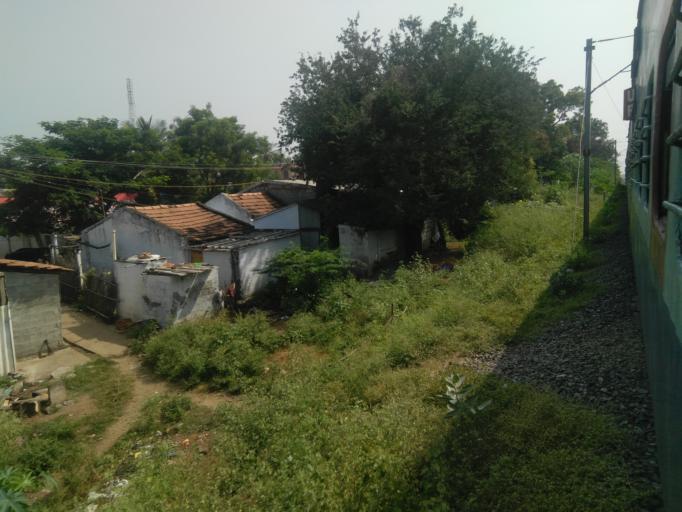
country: IN
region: Tamil Nadu
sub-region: Coimbatore
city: Mettupalayam
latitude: 11.2861
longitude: 76.9388
